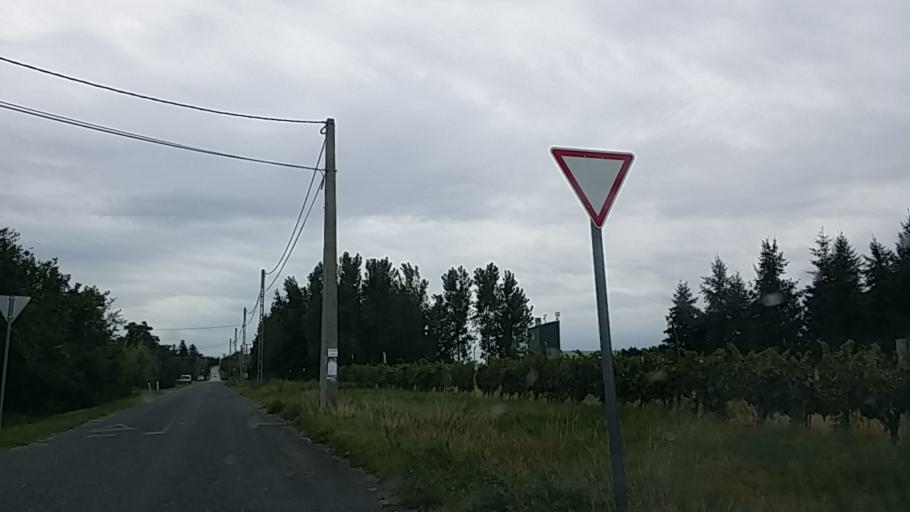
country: HU
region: Gyor-Moson-Sopron
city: Nagycenk
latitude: 47.6207
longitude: 16.7765
